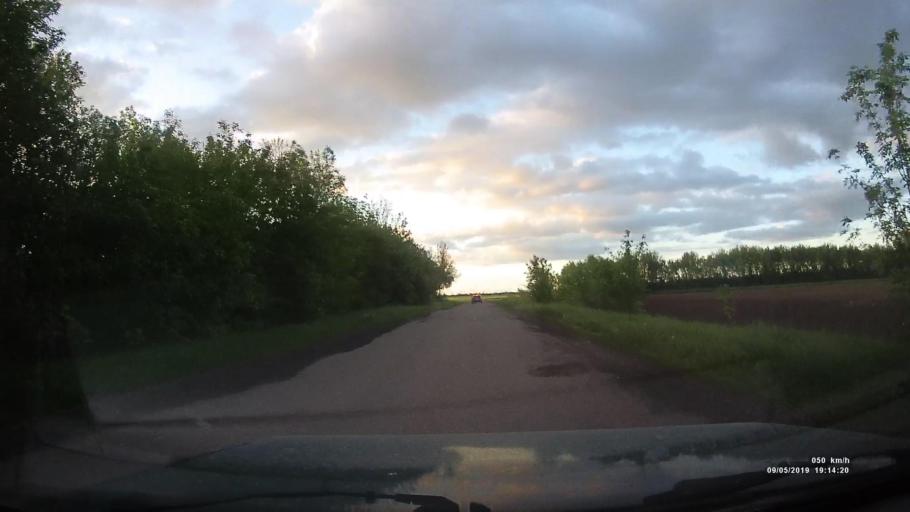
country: RU
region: Krasnodarskiy
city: Kanelovskaya
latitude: 46.7573
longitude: 39.2140
